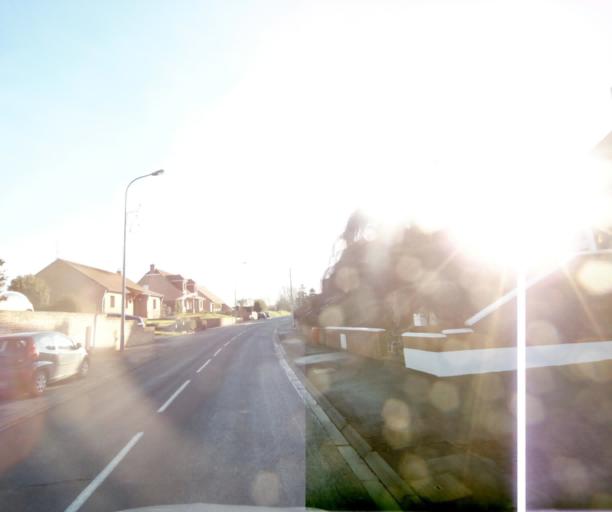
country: FR
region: Nord-Pas-de-Calais
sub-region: Departement du Nord
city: Saultain
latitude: 50.3340
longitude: 3.5747
